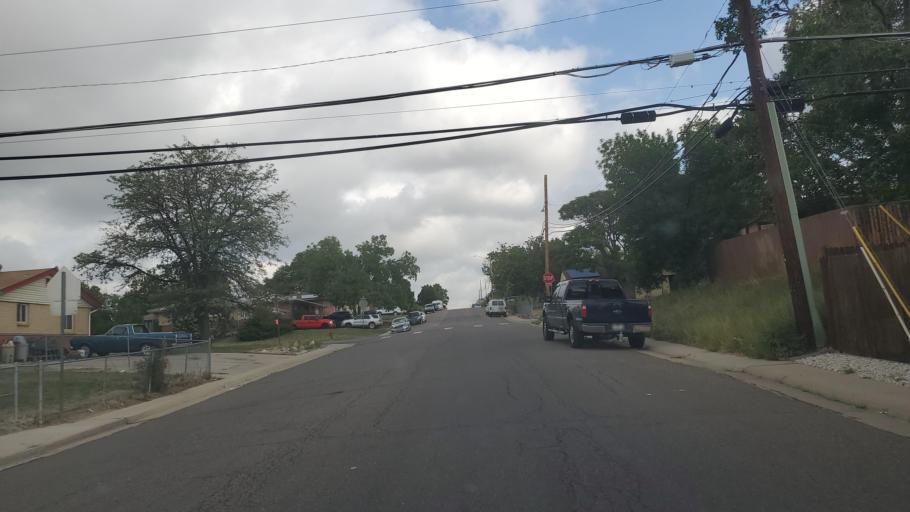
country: US
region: Colorado
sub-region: Adams County
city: Welby
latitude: 39.8488
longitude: -104.9684
